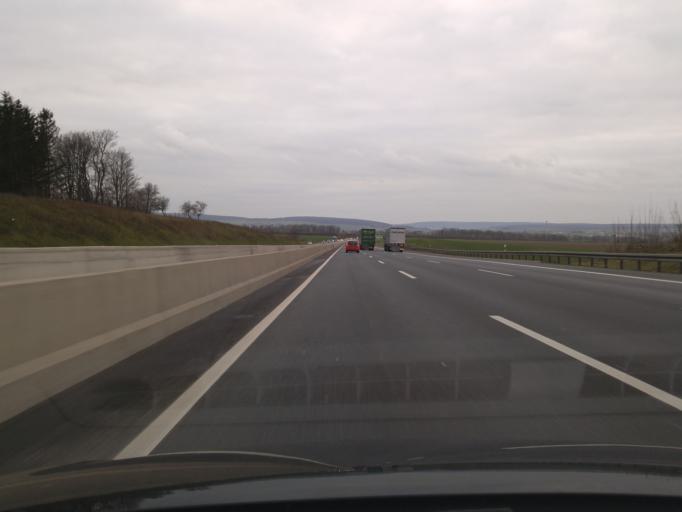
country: DE
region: Lower Saxony
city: Haverlah
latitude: 52.0286
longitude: 10.1717
